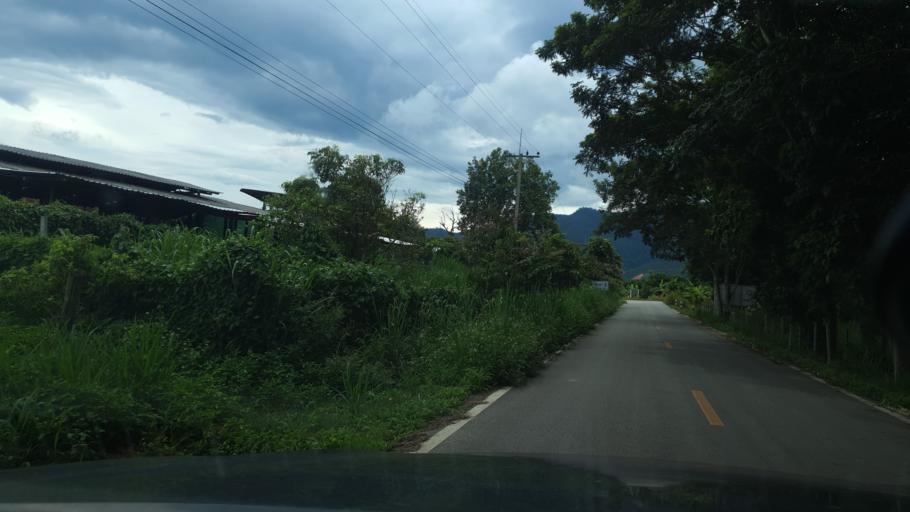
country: TH
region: Lamphun
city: Mae Tha
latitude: 18.5293
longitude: 99.2475
